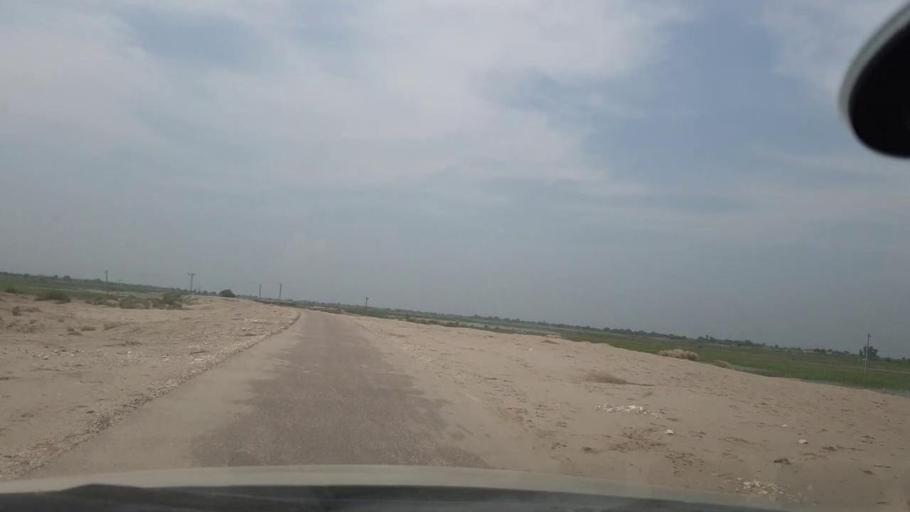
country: PK
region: Sindh
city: Jacobabad
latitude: 28.1400
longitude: 68.3525
